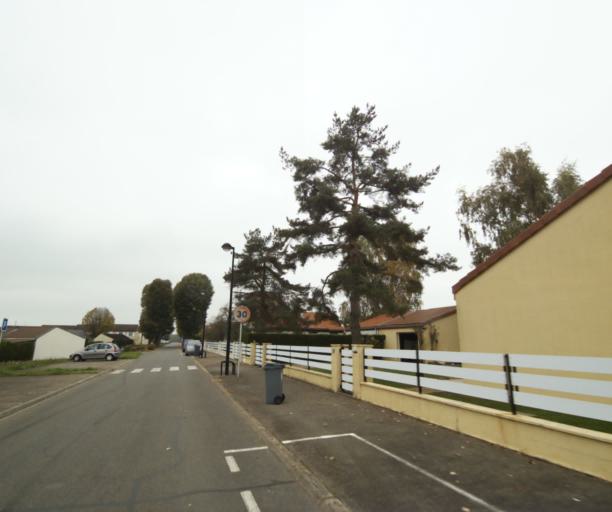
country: FR
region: Lorraine
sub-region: Departement de Meurthe-et-Moselle
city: Briey
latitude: 49.2396
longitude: 5.9334
